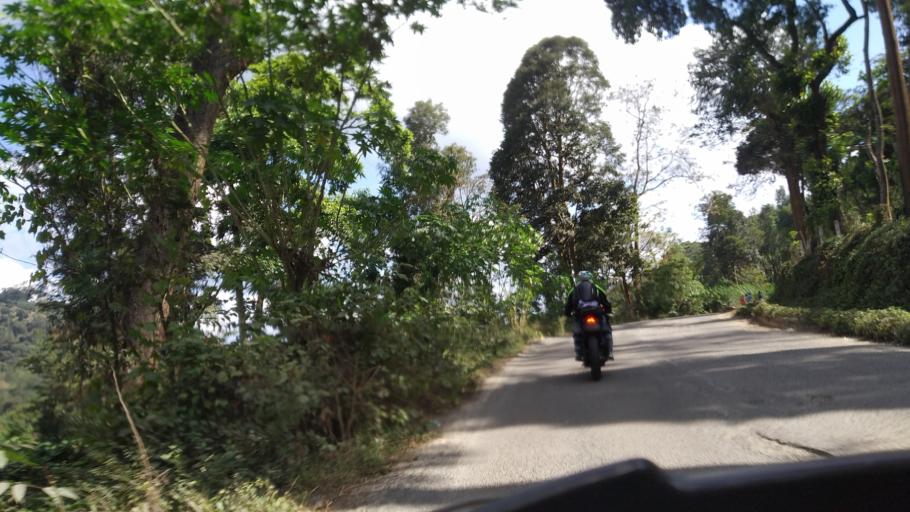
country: IN
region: Karnataka
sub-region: Kodagu
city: Ponnampet
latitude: 11.9631
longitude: 76.0587
